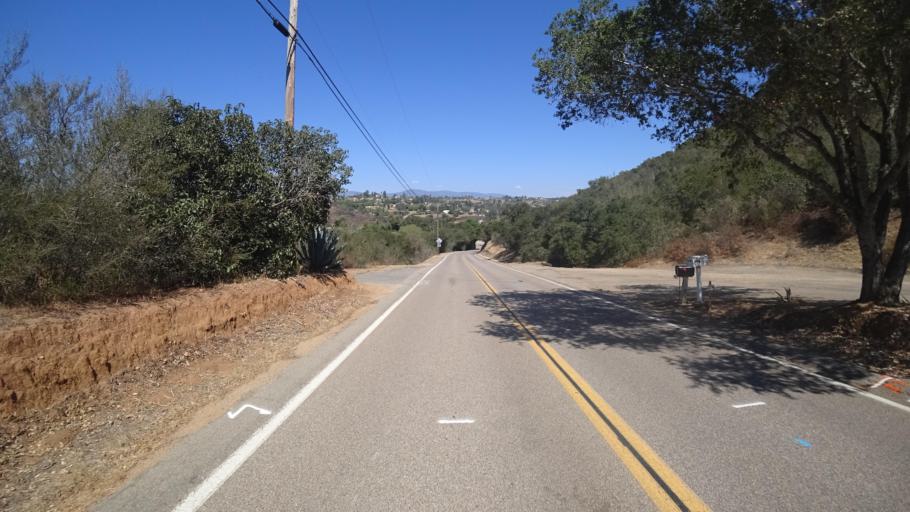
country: US
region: California
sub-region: San Diego County
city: Hidden Meadows
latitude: 33.2704
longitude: -117.0894
